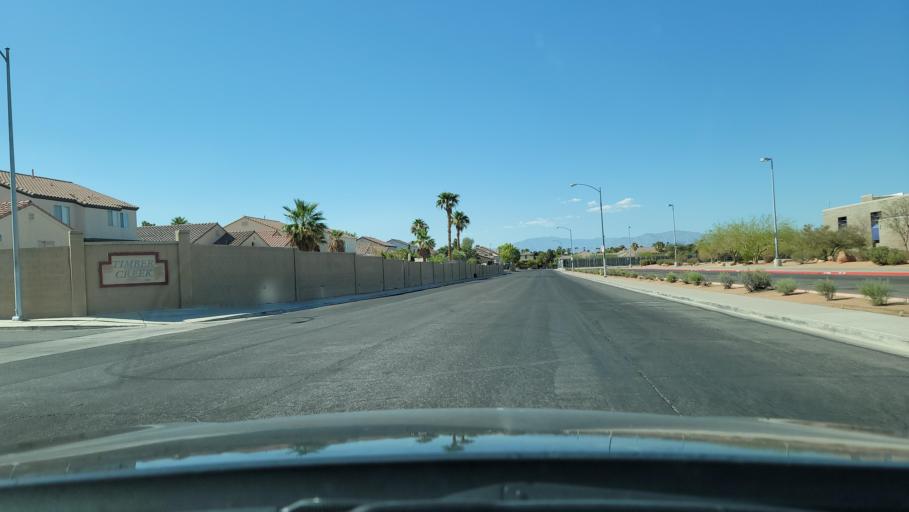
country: US
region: Nevada
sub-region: Clark County
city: Spring Valley
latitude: 36.0878
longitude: -115.2485
